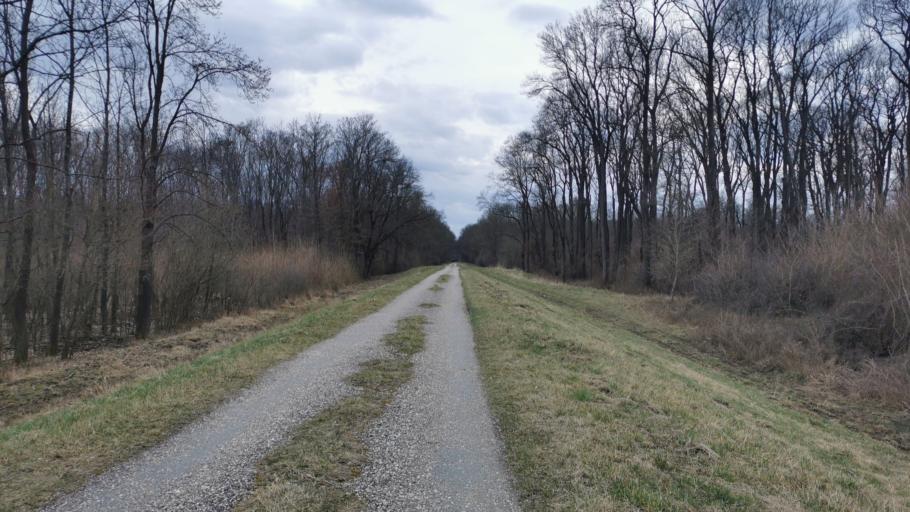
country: CZ
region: South Moravian
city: Hodonin
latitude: 48.8494
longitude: 17.1650
